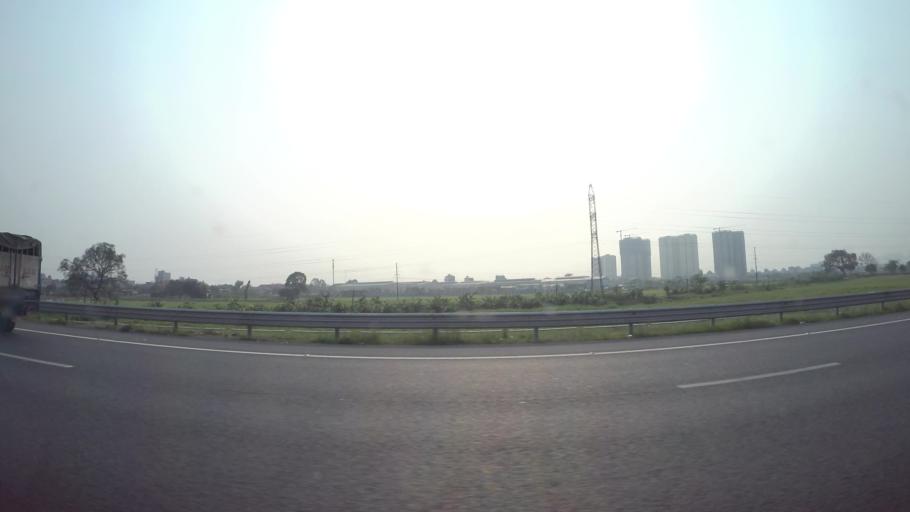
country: VN
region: Ha Noi
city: Van Dien
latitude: 20.9293
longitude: 105.8594
